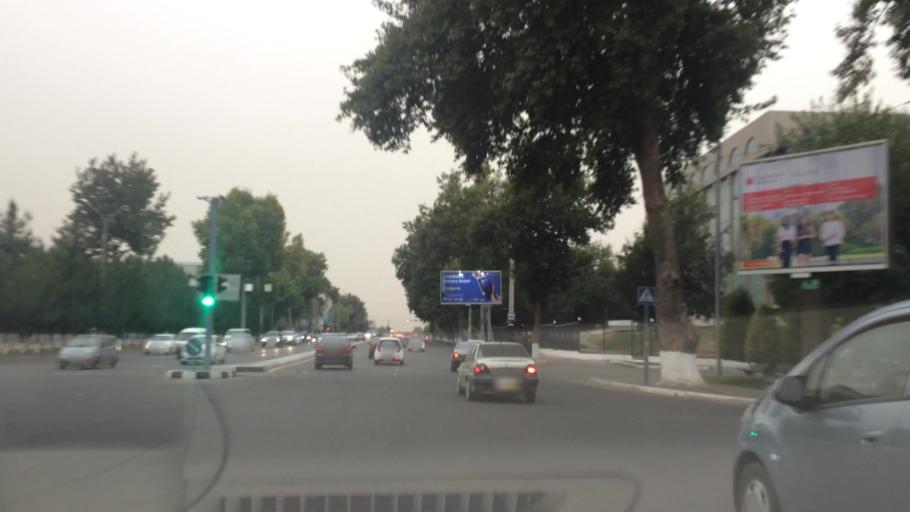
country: UZ
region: Toshkent Shahri
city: Tashkent
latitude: 41.3030
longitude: 69.2793
